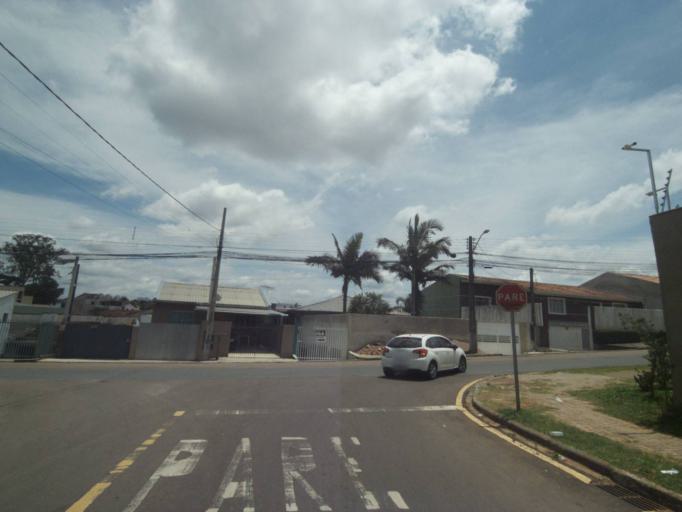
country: BR
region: Parana
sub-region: Curitiba
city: Curitiba
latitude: -25.4603
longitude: -49.3472
